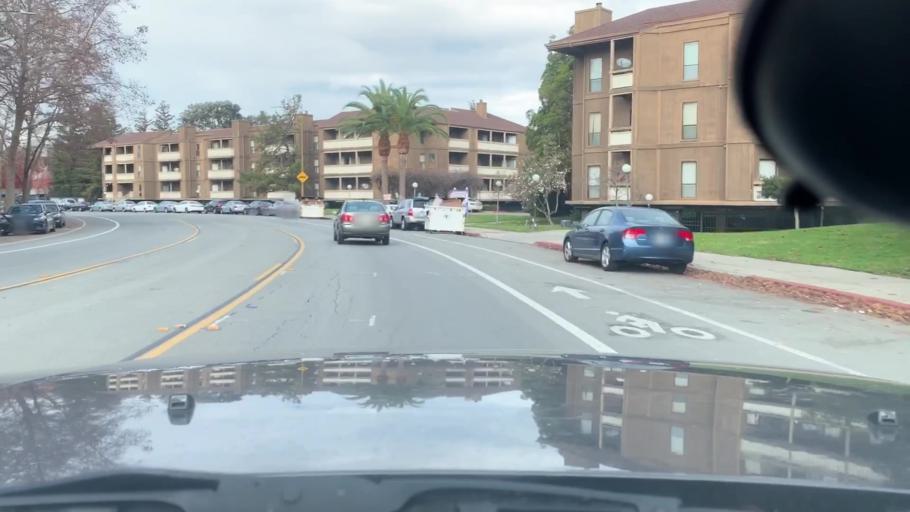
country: US
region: California
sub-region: Santa Clara County
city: Campbell
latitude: 37.3025
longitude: -121.9771
